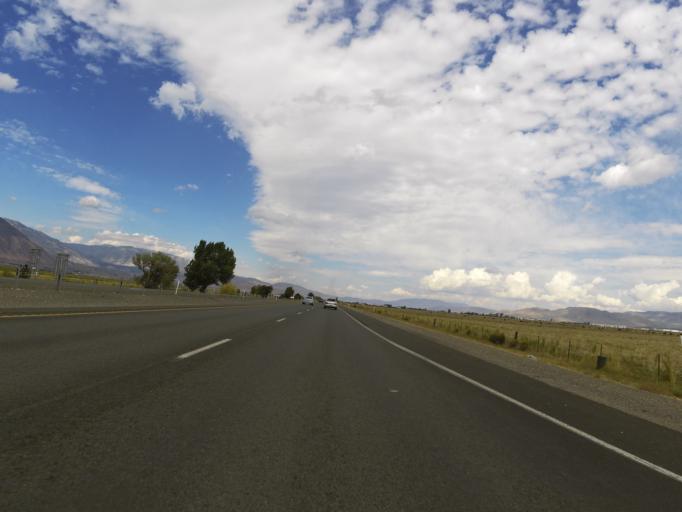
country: US
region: Nevada
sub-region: Douglas County
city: Minden
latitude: 38.9762
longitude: -119.7794
